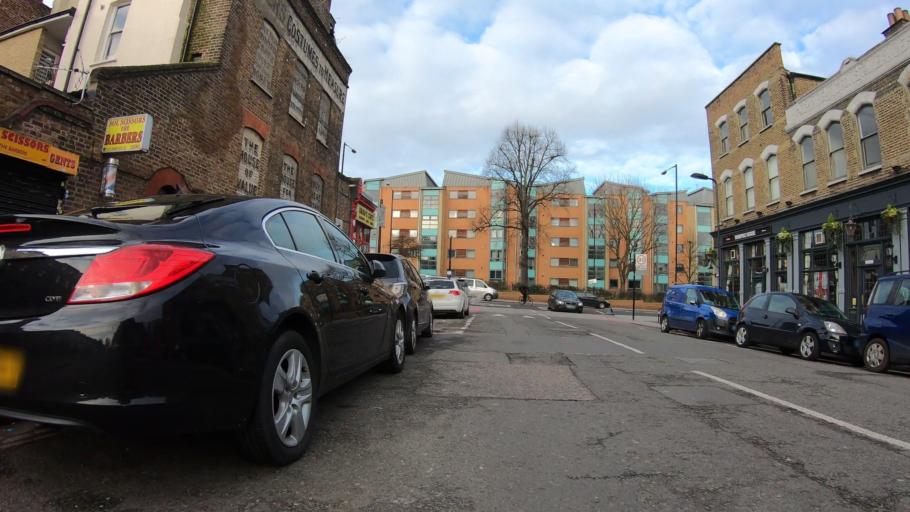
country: GB
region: England
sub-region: Greater London
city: Hackney
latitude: 51.5708
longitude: -0.0579
